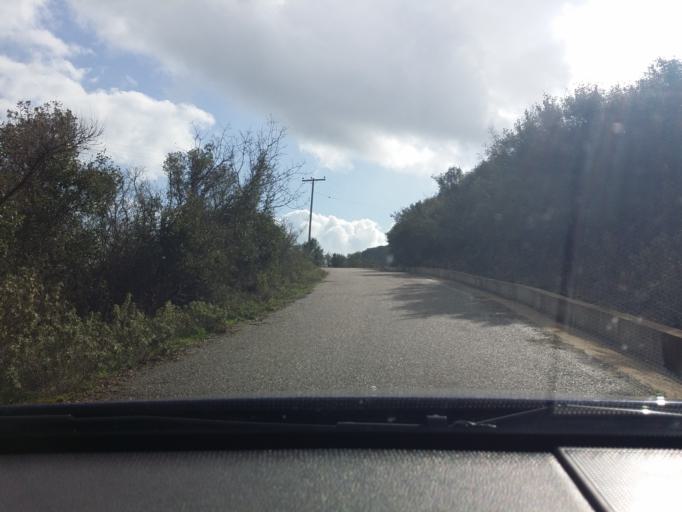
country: GR
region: West Greece
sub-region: Nomos Aitolias kai Akarnanias
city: Fitiai
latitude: 38.6625
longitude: 21.1922
